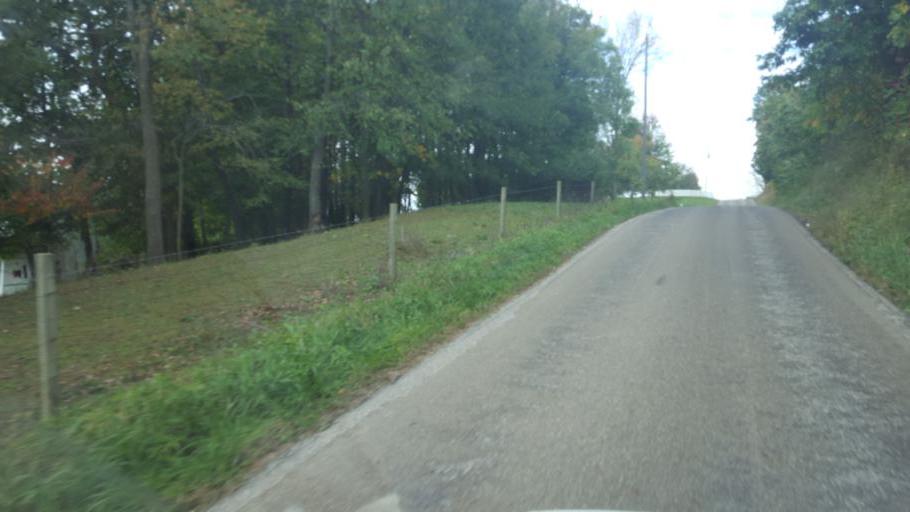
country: US
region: Ohio
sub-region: Holmes County
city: Millersburg
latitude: 40.5781
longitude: -81.8013
